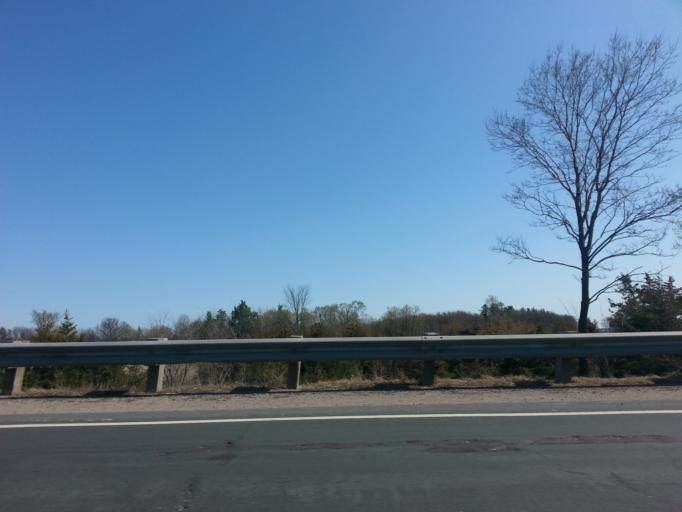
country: US
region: Wisconsin
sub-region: Pepin County
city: Durand
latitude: 44.7131
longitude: -91.9403
